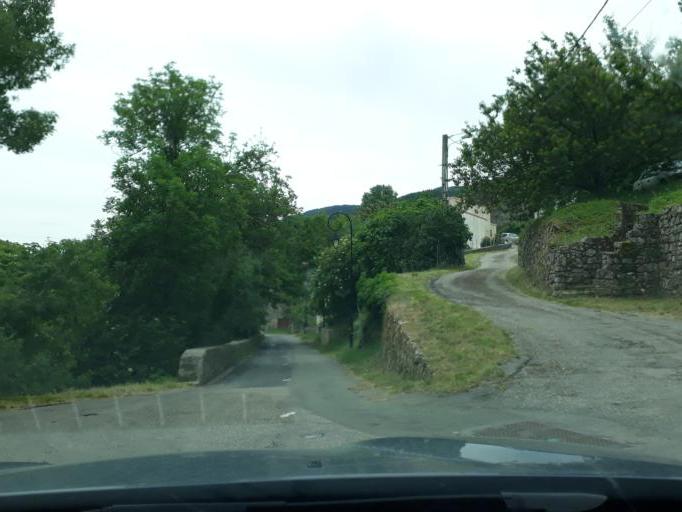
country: FR
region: Languedoc-Roussillon
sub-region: Departement de l'Herault
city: Lodeve
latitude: 43.7794
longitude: 3.2882
